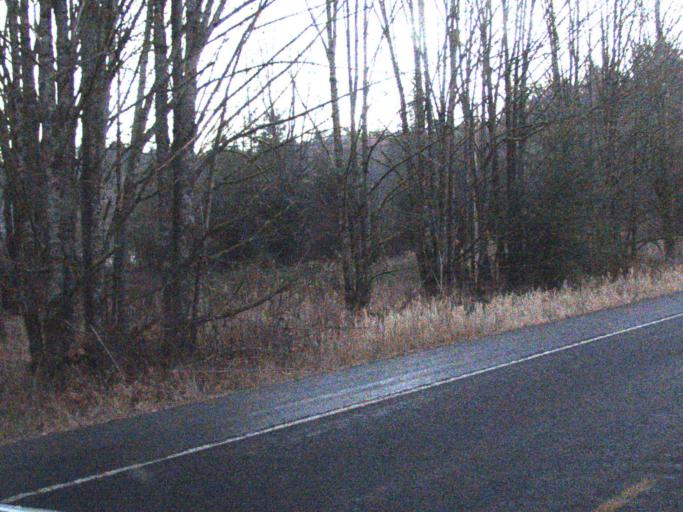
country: US
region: Washington
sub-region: Skagit County
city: Sedro-Woolley
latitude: 48.5298
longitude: -121.9897
